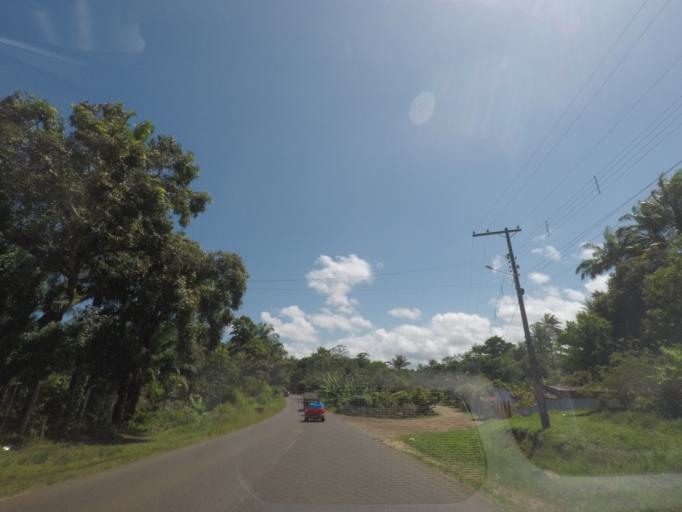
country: BR
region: Bahia
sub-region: Taperoa
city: Taperoa
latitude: -13.4593
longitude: -39.0892
